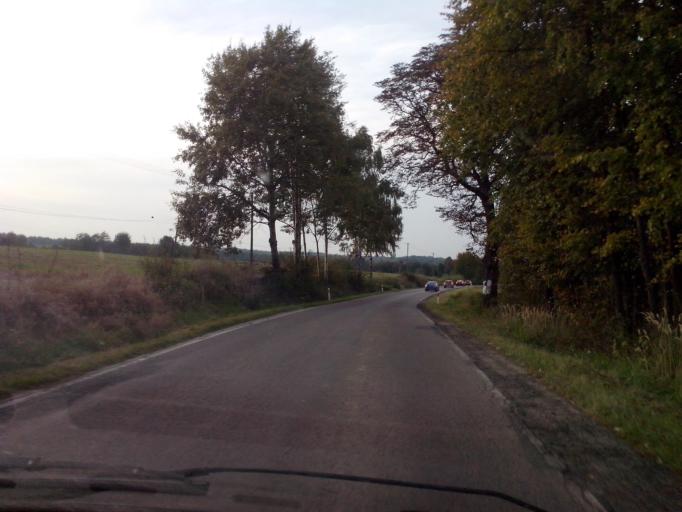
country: PL
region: Subcarpathian Voivodeship
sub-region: Powiat strzyzowski
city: Jawornik
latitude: 49.8189
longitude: 21.8355
